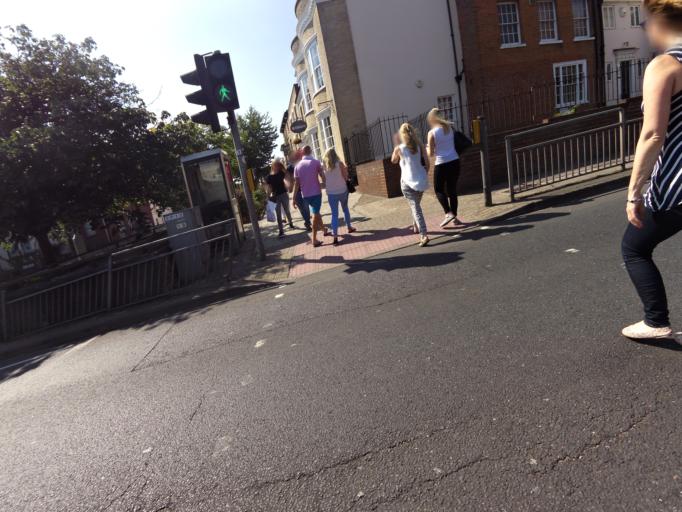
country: GB
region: England
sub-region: Essex
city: Colchester
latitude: 51.8878
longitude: 0.8935
